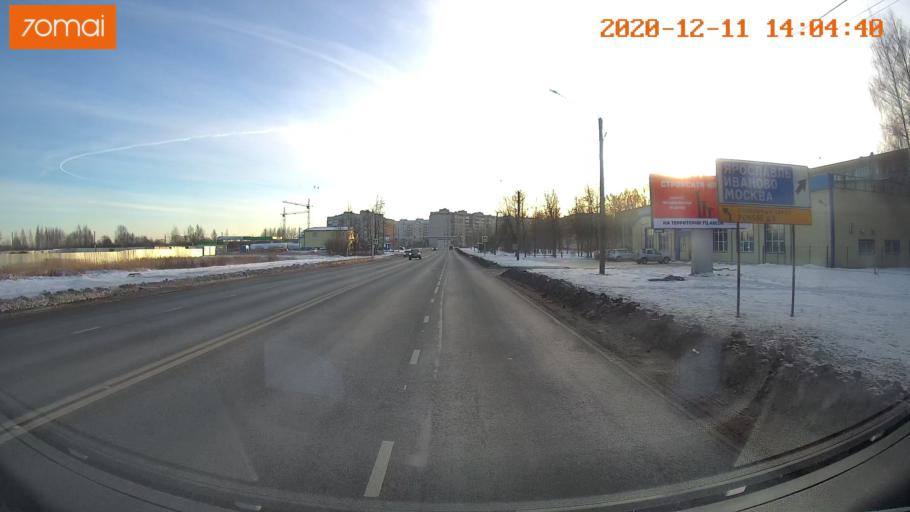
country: RU
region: Kostroma
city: Oktyabr'skiy
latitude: 57.7532
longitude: 41.0164
